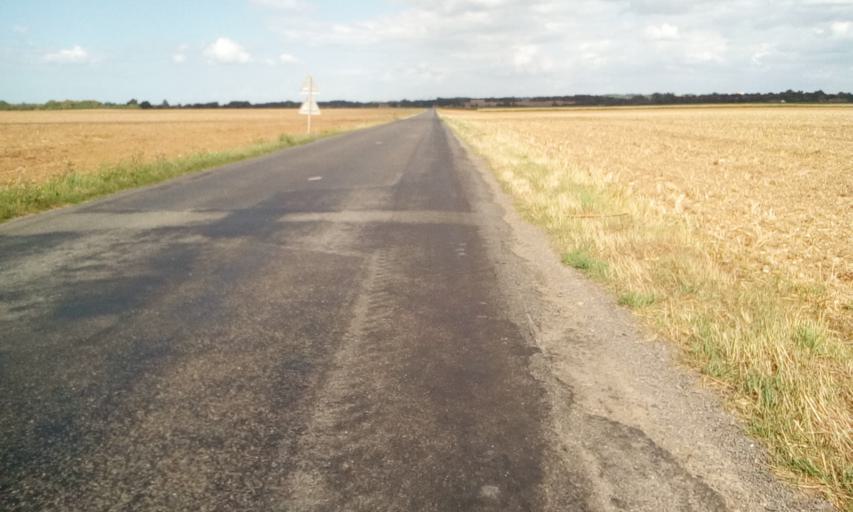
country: FR
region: Lower Normandy
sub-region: Departement du Calvados
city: Bellengreville
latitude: 49.0943
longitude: -0.2101
